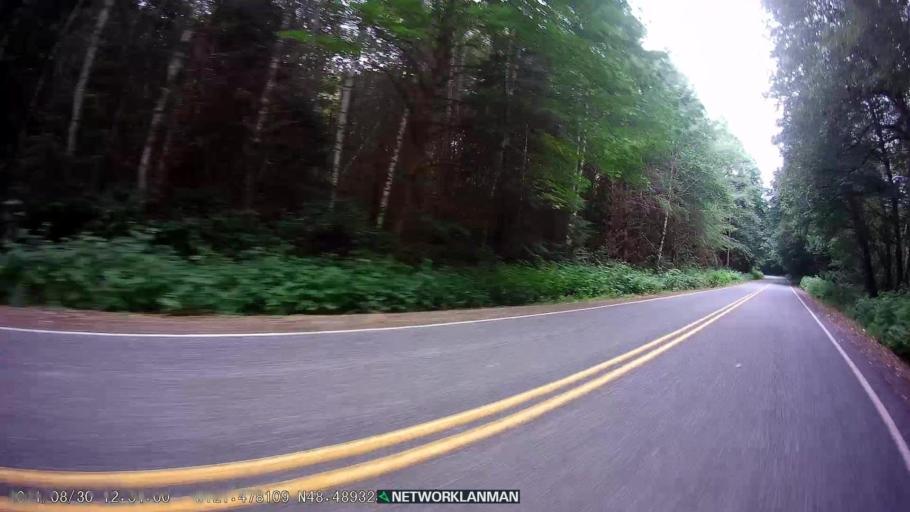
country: US
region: Washington
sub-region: Snohomish County
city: Darrington
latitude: 48.4892
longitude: -121.4786
